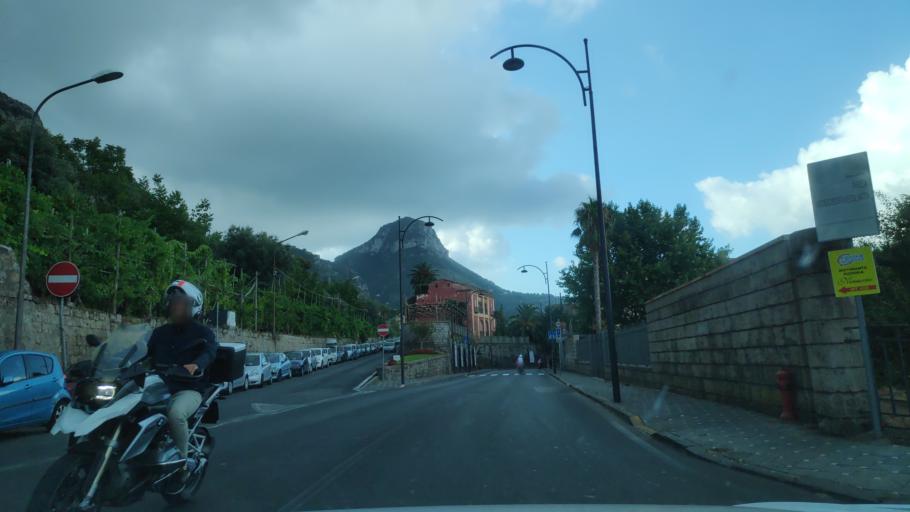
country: IT
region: Campania
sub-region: Provincia di Napoli
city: Meta
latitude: 40.6413
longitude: 14.4184
